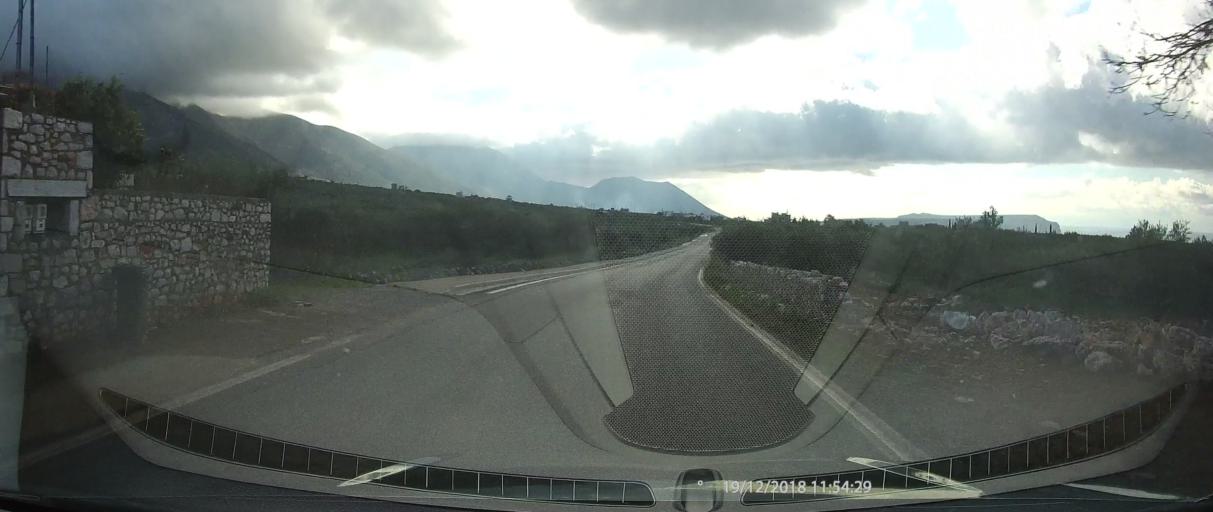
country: GR
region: Peloponnese
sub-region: Nomos Lakonias
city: Gytheio
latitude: 36.6180
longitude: 22.3908
